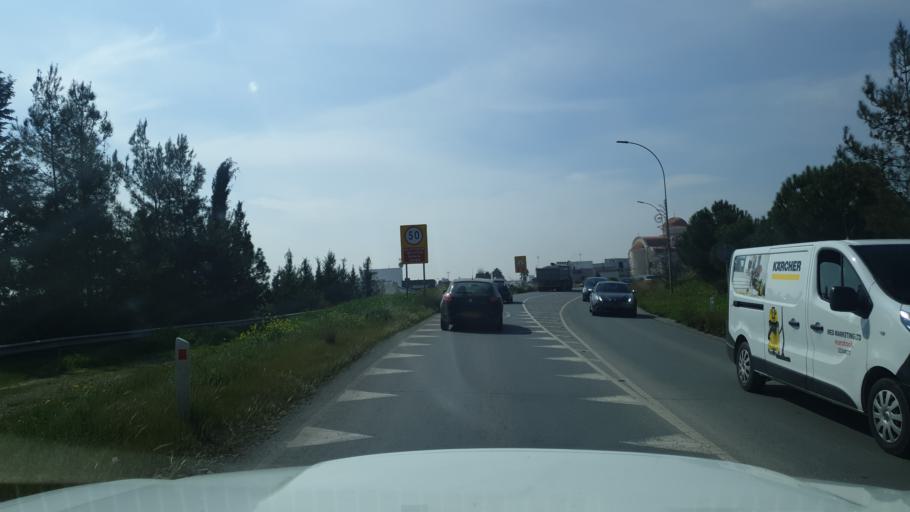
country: CY
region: Lefkosia
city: Nicosia
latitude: 35.1459
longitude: 33.3065
